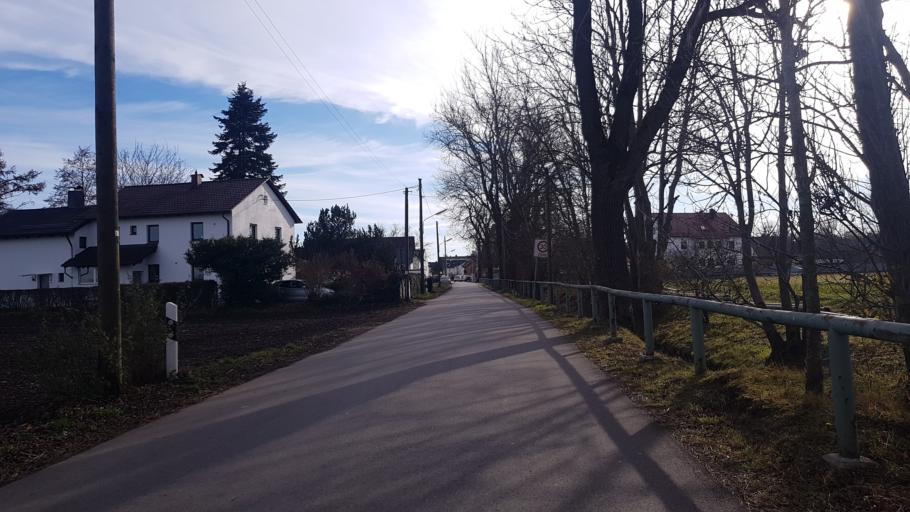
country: DE
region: Bavaria
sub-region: Upper Bavaria
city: Oberschleissheim
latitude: 48.2209
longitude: 11.5278
